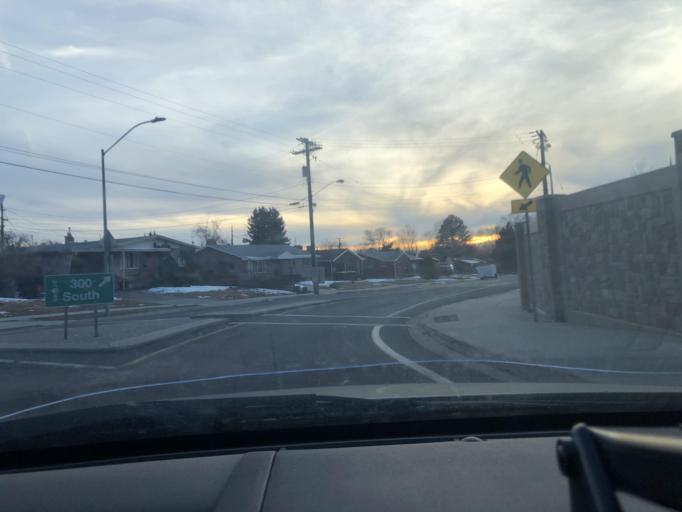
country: US
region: Utah
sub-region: Utah County
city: Provo
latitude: 40.2299
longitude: -111.6353
